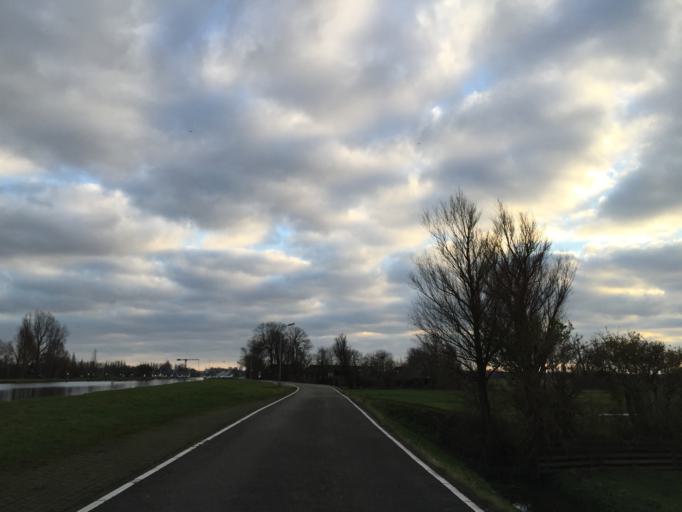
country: NL
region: South Holland
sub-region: Gemeente Schiedam
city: Schiedam
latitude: 51.9676
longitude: 4.3894
